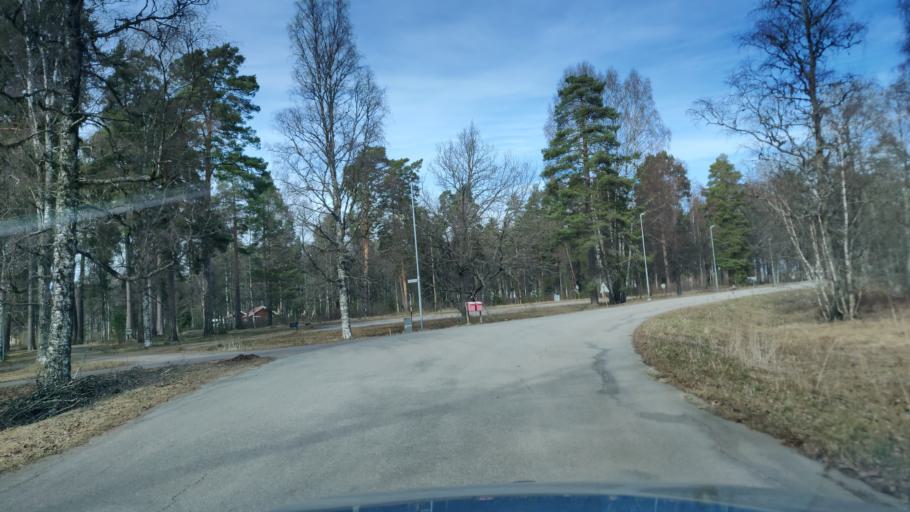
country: SE
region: Vaermland
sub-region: Hagfors Kommun
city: Hagfors
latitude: 60.0200
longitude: 13.6192
